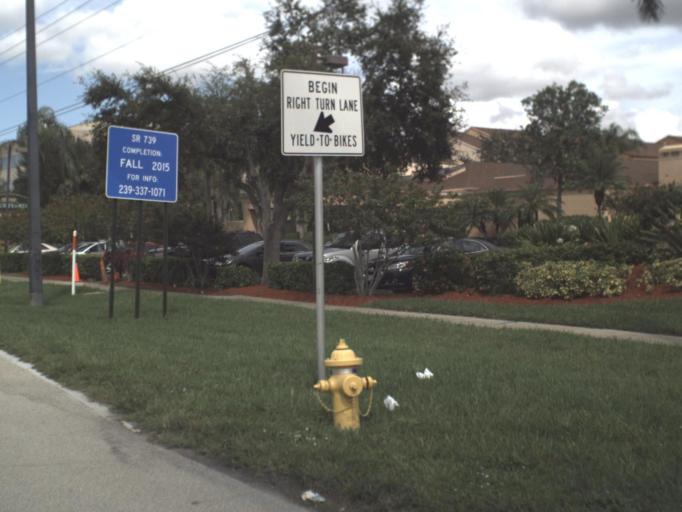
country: US
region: Florida
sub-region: Lee County
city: Fort Myers
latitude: 26.5978
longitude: -81.8504
